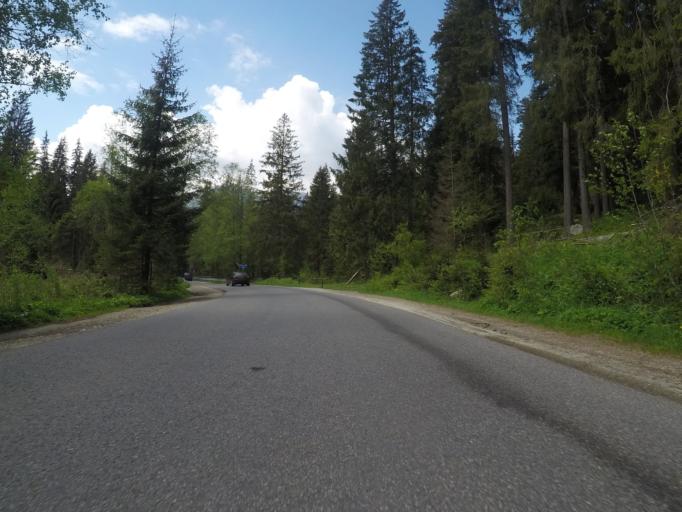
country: PL
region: Lesser Poland Voivodeship
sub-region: Powiat tatrzanski
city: Bukowina Tatrzanska
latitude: 49.2637
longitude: 20.1126
